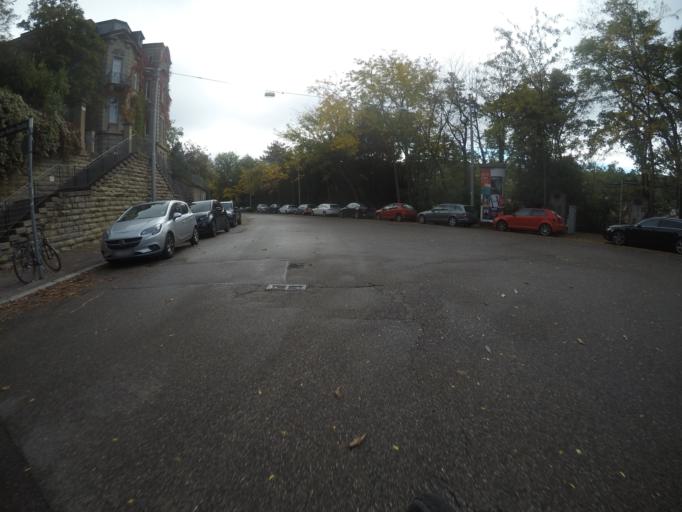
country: DE
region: Baden-Wuerttemberg
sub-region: Regierungsbezirk Stuttgart
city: Stuttgart
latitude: 48.7658
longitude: 9.1631
